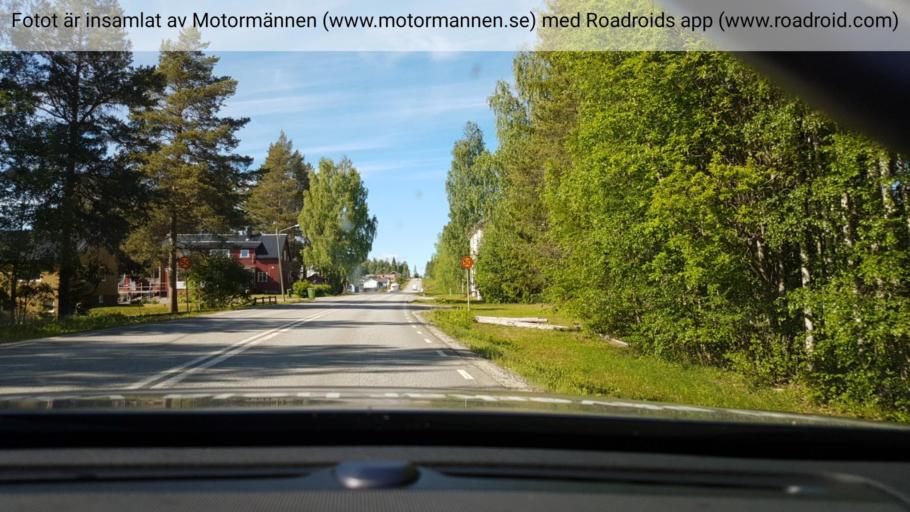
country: SE
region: Vaesterbotten
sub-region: Lycksele Kommun
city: Lycksele
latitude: 64.7377
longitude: 18.6693
